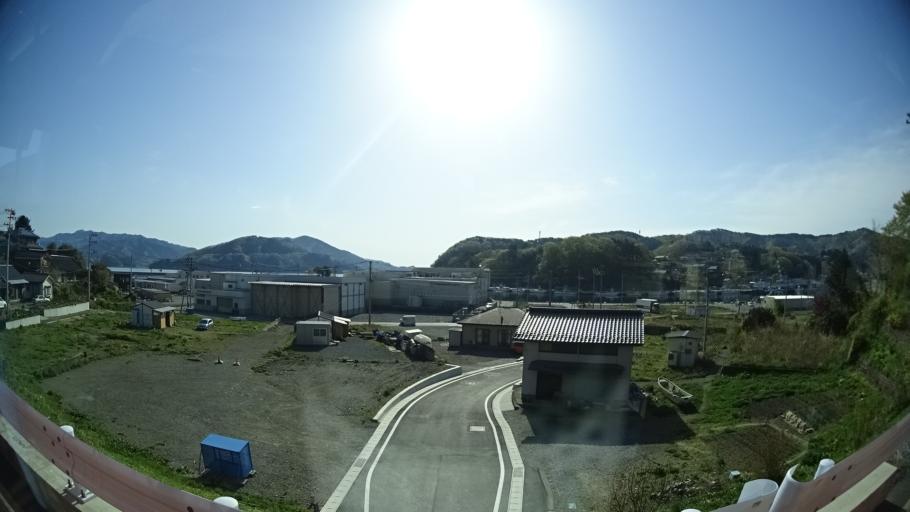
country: JP
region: Iwate
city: Ofunato
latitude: 39.0194
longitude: 141.7135
